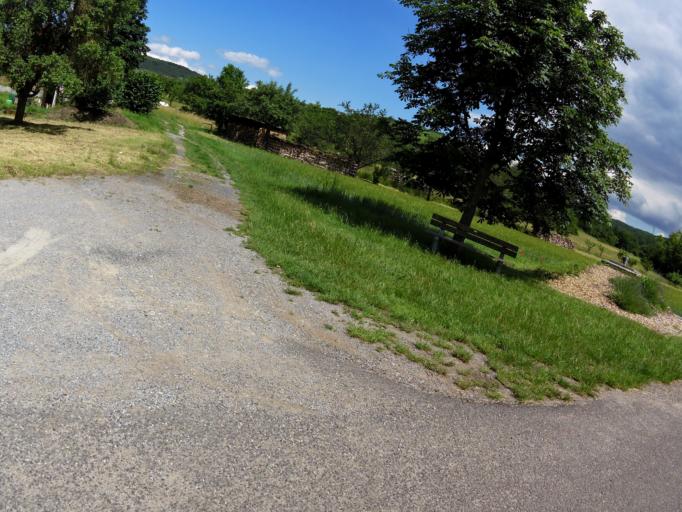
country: DE
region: Bavaria
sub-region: Regierungsbezirk Unterfranken
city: Thungersheim
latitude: 49.8761
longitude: 9.8513
